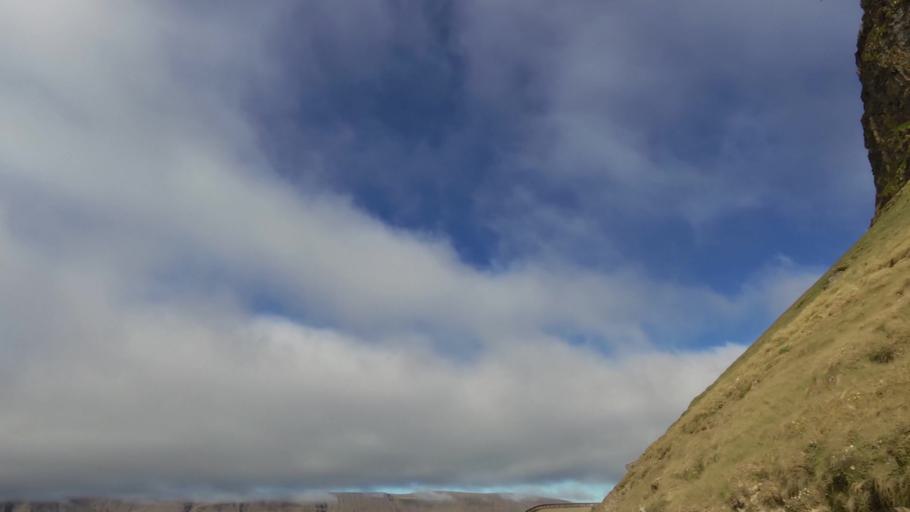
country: IS
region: West
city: Olafsvik
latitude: 65.5822
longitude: -24.0926
